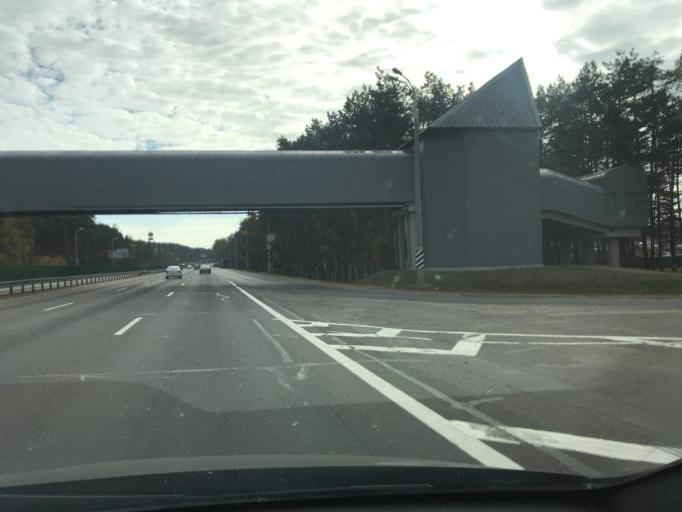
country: BY
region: Minsk
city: Vyaliki Trastsyanets
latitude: 53.8903
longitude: 27.6937
